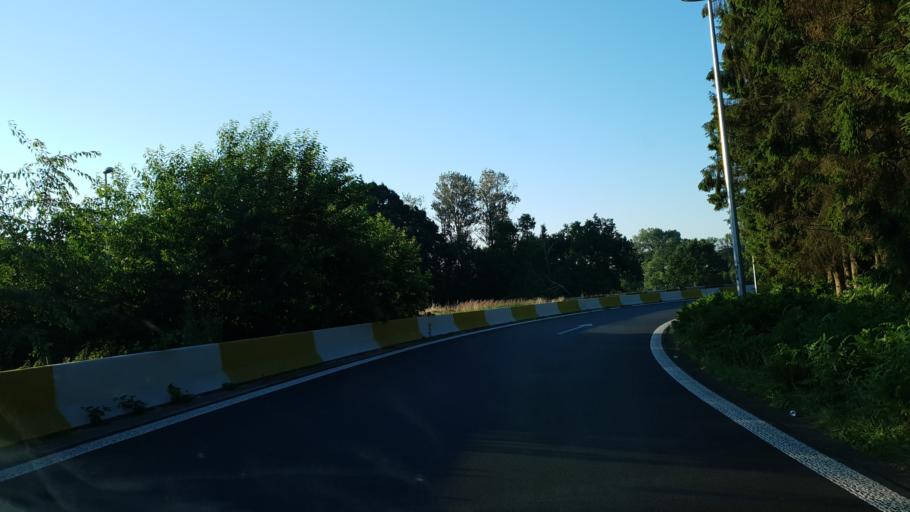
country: BE
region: Flanders
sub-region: Provincie Antwerpen
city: Beerse
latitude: 51.2857
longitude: 4.8571
